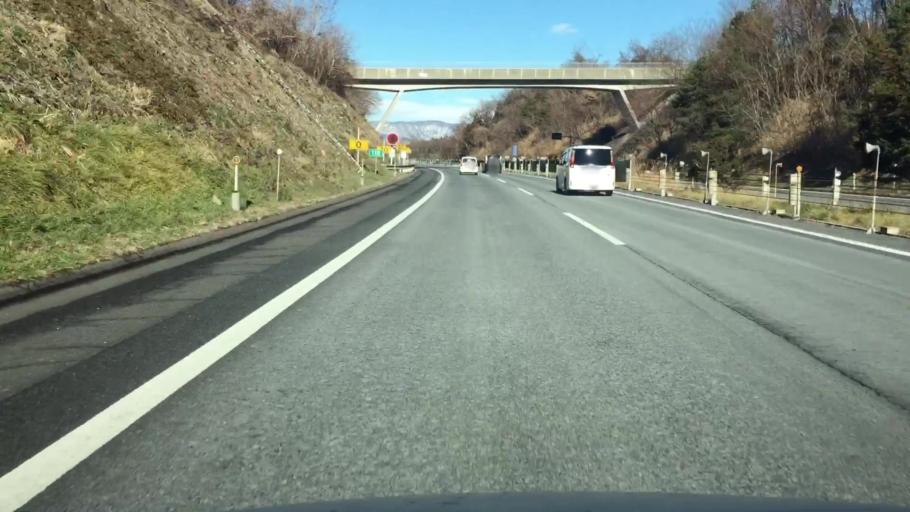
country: JP
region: Gunma
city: Numata
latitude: 36.5927
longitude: 139.0663
